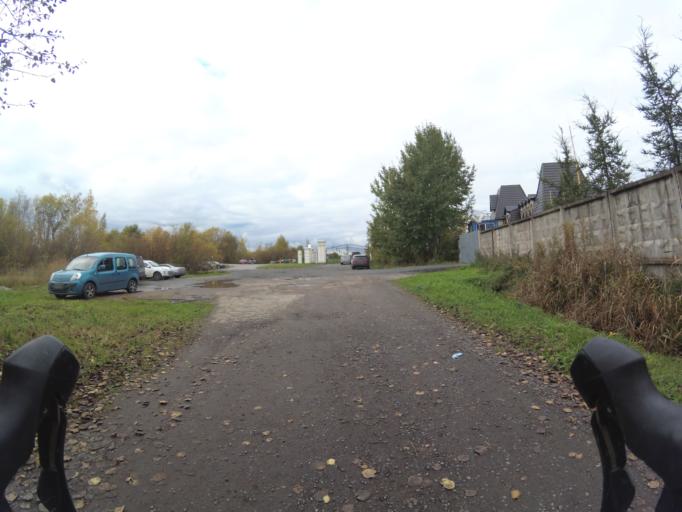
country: RU
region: St.-Petersburg
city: Lakhtinskiy
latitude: 59.9977
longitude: 30.1613
